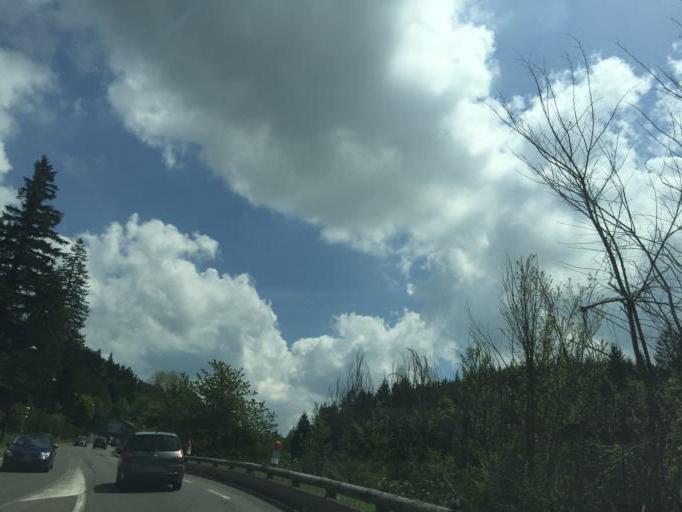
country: FR
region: Rhone-Alpes
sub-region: Departement de la Loire
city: Saint-Genest-Malifaux
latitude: 45.3799
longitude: 4.4391
